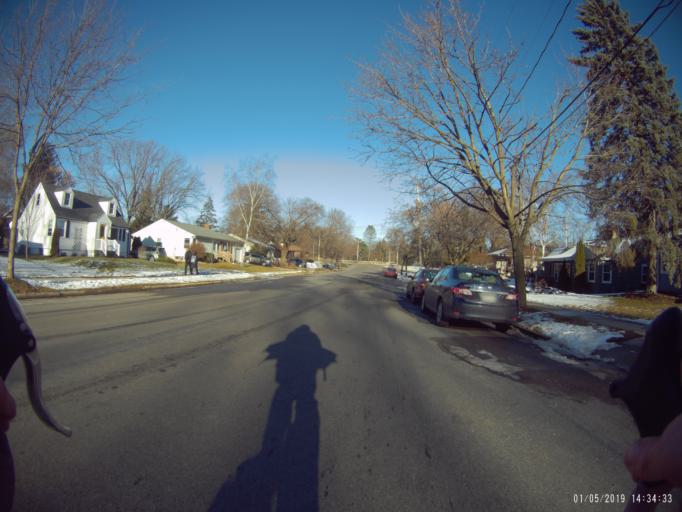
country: US
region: Wisconsin
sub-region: Dane County
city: Shorewood Hills
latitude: 43.0549
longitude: -89.4398
